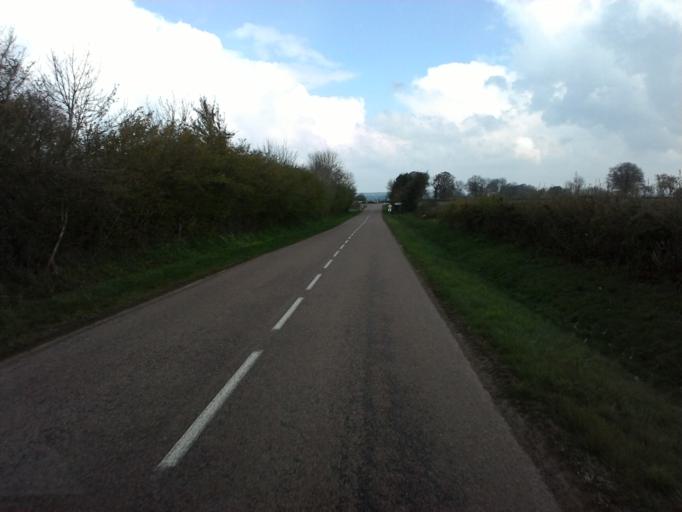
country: FR
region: Bourgogne
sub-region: Departement de la Cote-d'Or
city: Saulieu
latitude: 47.2656
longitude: 4.2218
